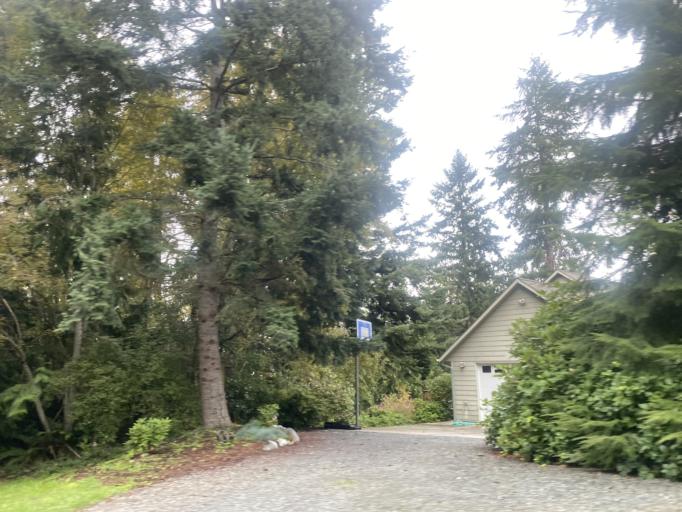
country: US
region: Washington
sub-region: Island County
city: Freeland
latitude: 48.0874
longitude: -122.5641
